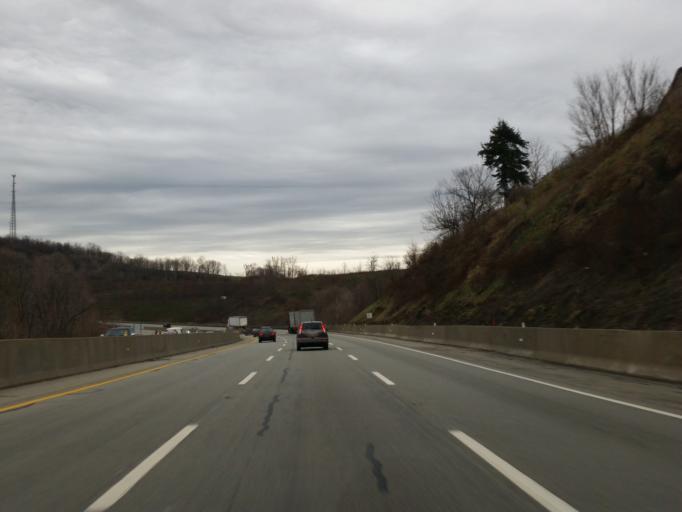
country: US
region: Pennsylvania
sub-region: Fayette County
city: Bear Rocks
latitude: 40.1072
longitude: -79.3749
